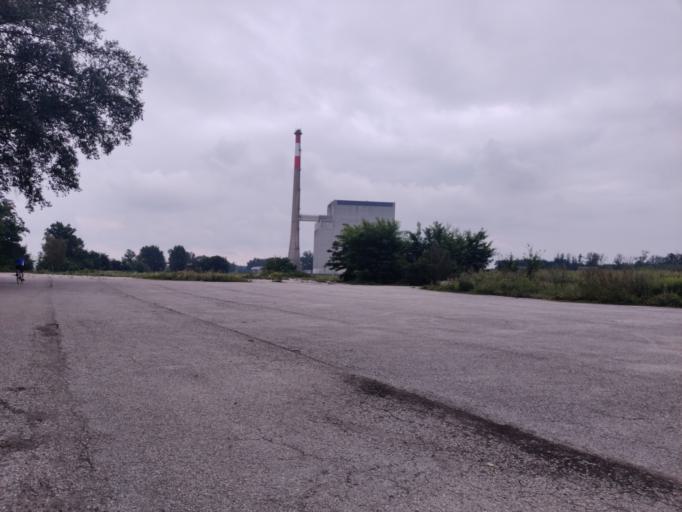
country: AT
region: Lower Austria
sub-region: Politischer Bezirk Tulln
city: Atzenbrugg
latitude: 48.3577
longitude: 15.8815
